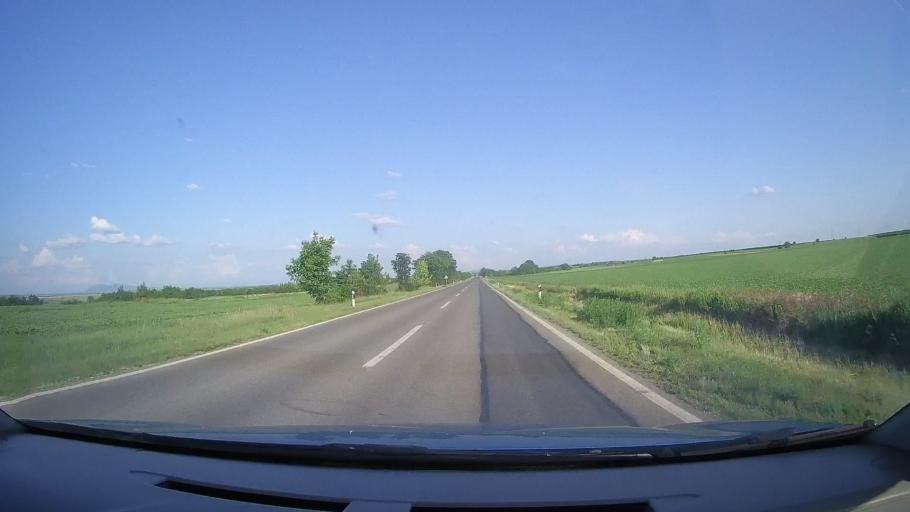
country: RS
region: Autonomna Pokrajina Vojvodina
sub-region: Juznobanatski Okrug
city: Alibunar
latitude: 45.0611
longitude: 20.9856
